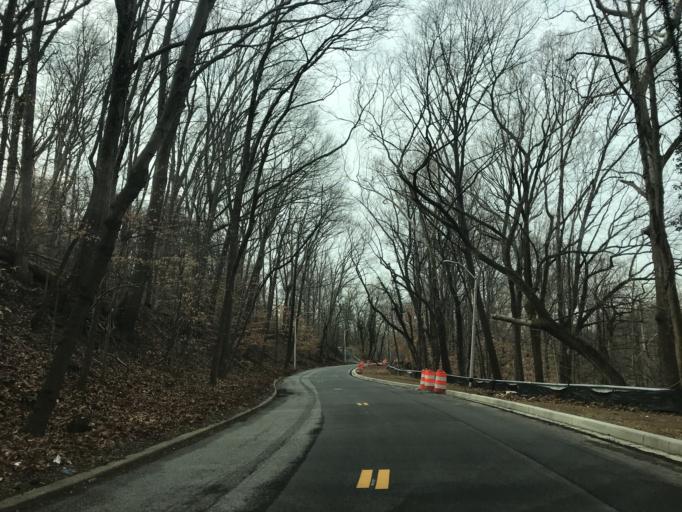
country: US
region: Maryland
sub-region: Baltimore County
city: Pikesville
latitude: 39.3669
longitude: -76.6658
